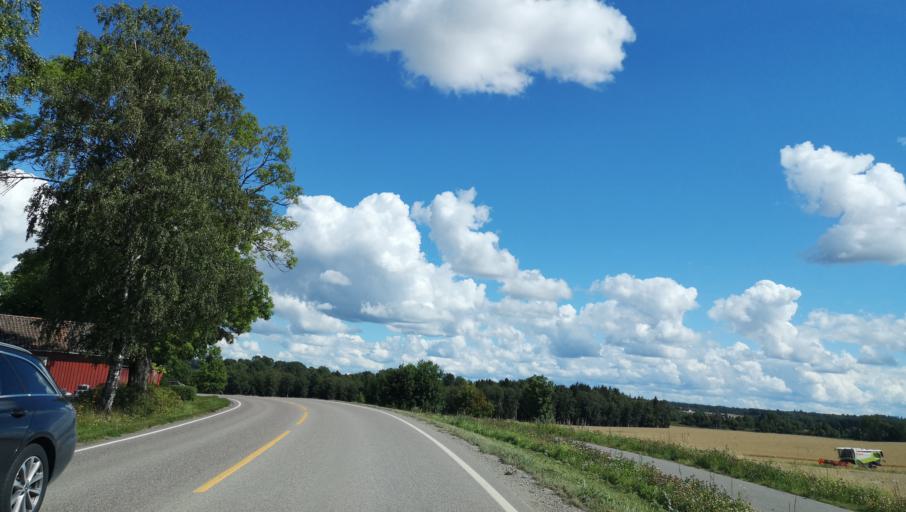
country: NO
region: Akershus
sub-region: Vestby
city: Vestby
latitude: 59.6596
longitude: 10.7317
